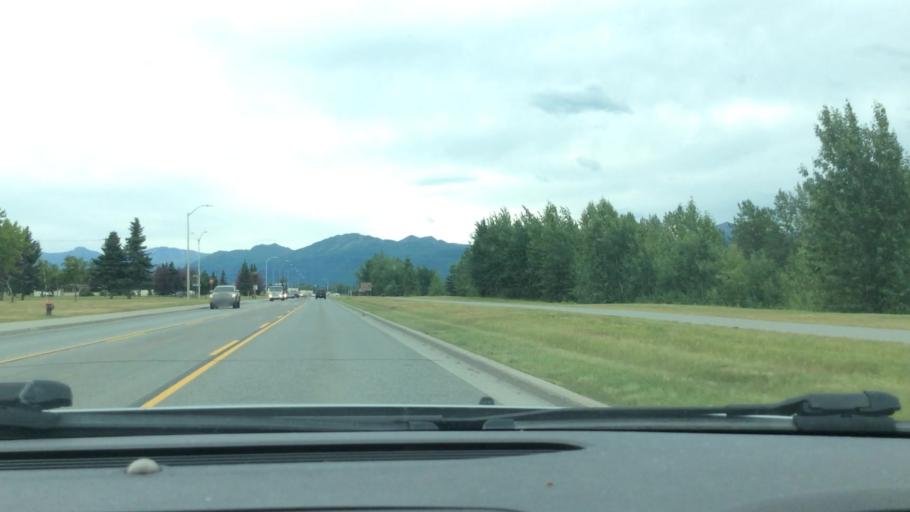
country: US
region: Alaska
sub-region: Anchorage Municipality
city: Anchorage
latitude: 61.2387
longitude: -149.8110
